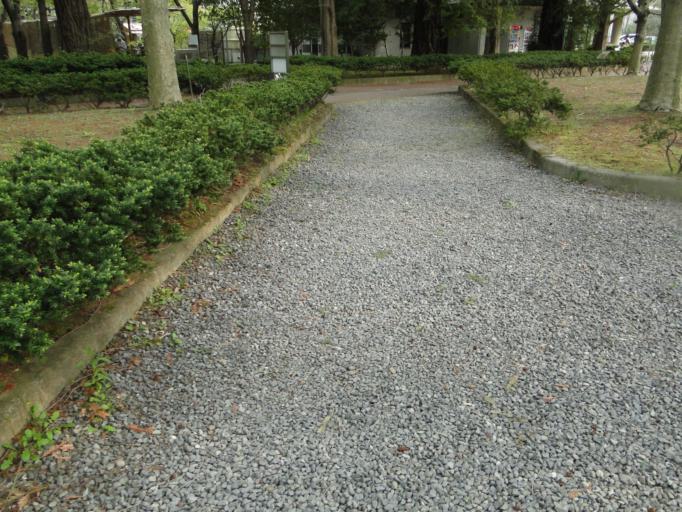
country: JP
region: Ibaraki
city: Naka
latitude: 36.0999
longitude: 140.1110
